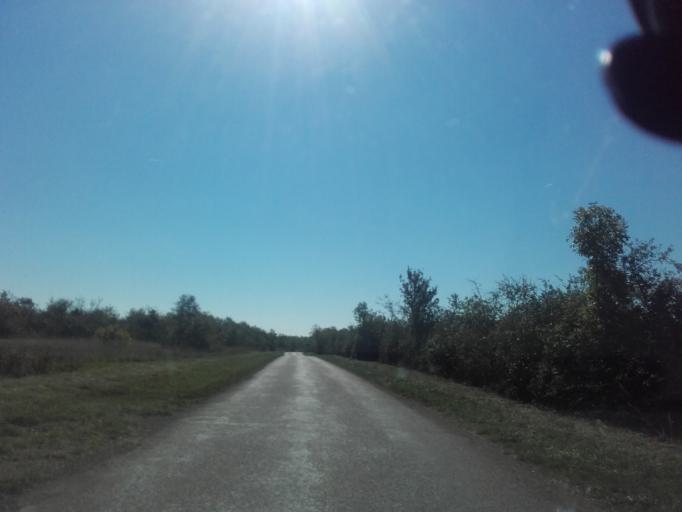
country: FR
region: Bourgogne
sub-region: Departement de la Cote-d'Or
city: Nolay
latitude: 46.9956
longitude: 4.6955
